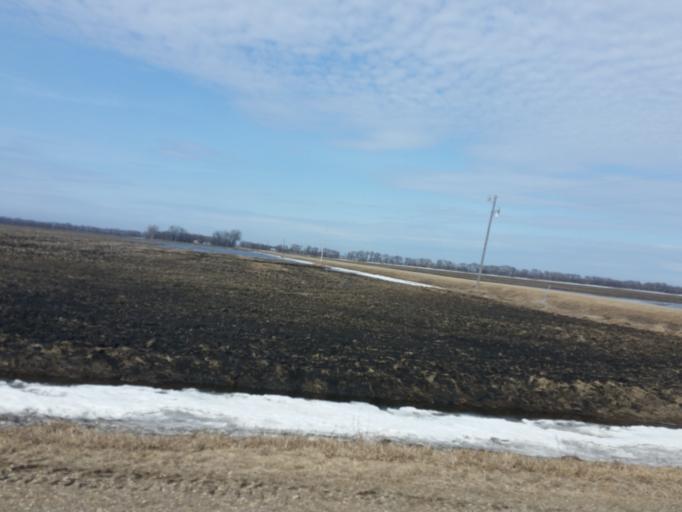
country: US
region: North Dakota
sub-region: Walsh County
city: Grafton
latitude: 48.4265
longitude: -97.2126
